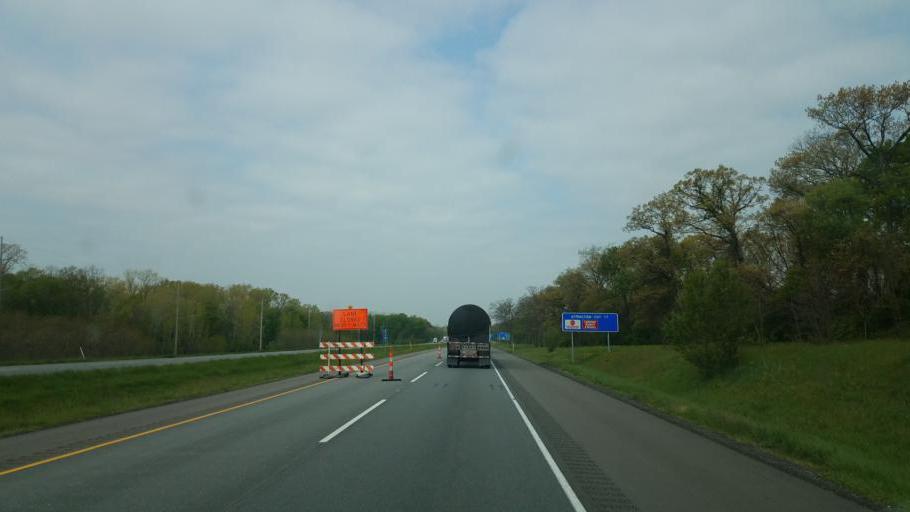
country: US
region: Indiana
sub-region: Saint Joseph County
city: Georgetown
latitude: 41.7163
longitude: -86.2214
